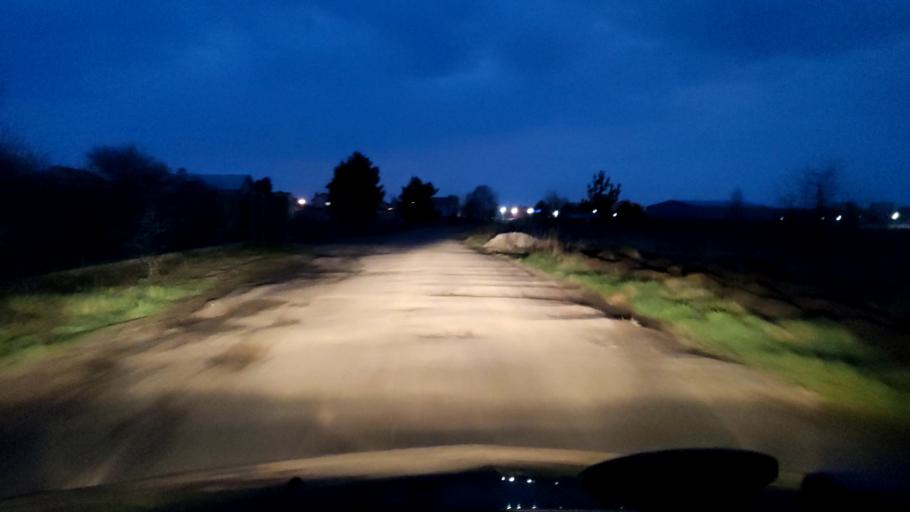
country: RU
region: Voronezj
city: Pridonskoy
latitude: 51.6348
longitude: 39.1071
